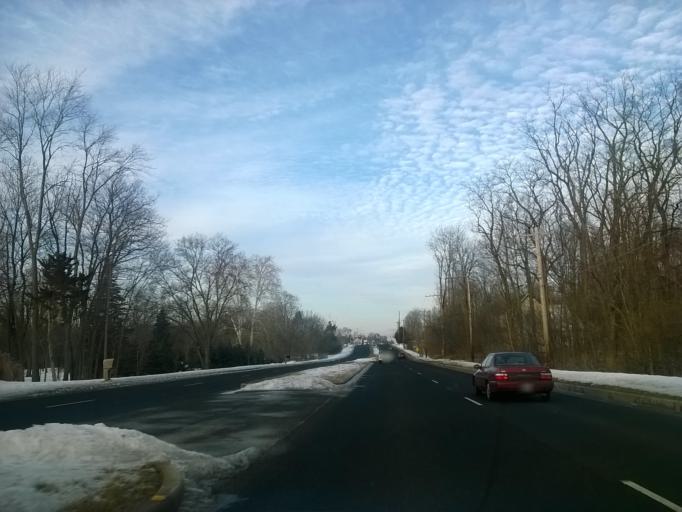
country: US
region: Indiana
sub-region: Hamilton County
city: Carmel
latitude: 40.0003
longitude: -86.0844
